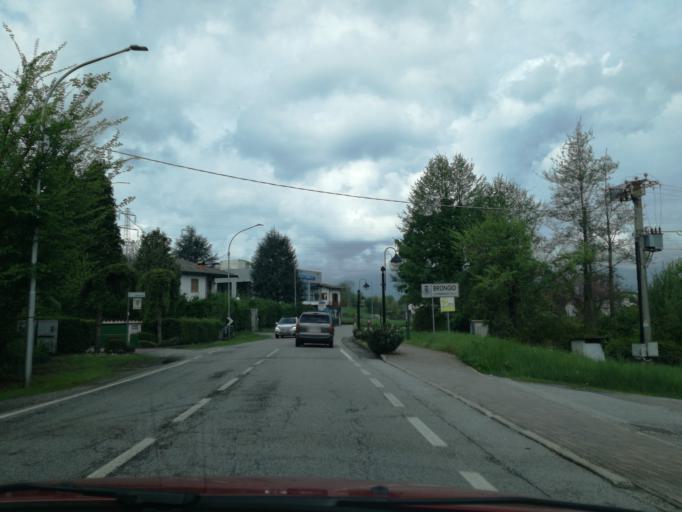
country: IT
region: Lombardy
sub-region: Provincia di Lecco
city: Barzago
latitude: 45.7603
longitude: 9.3148
